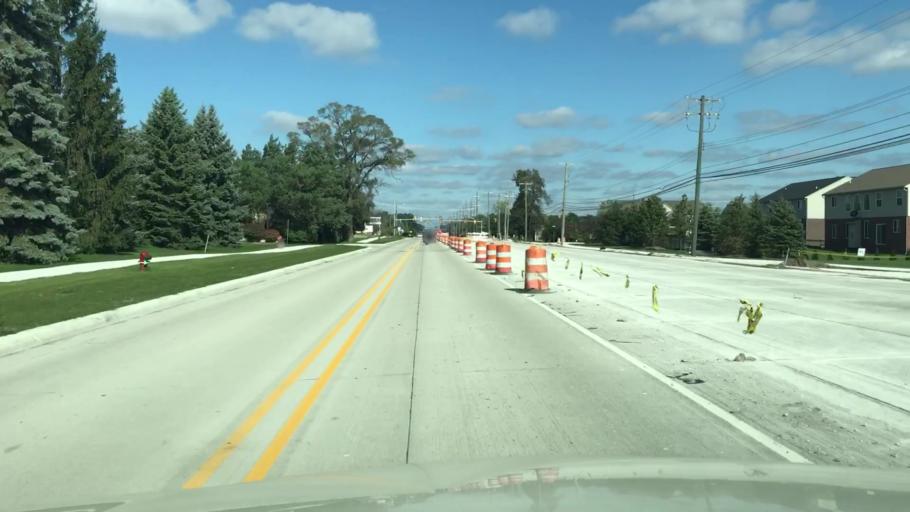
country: US
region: Michigan
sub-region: Oakland County
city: Troy
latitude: 42.6047
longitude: -83.0906
